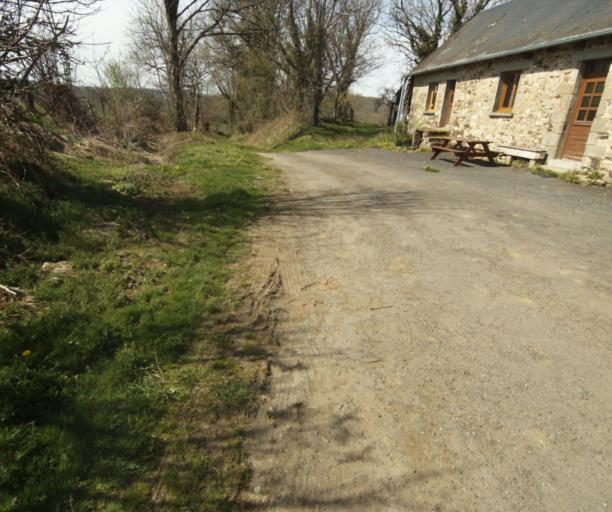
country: FR
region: Limousin
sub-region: Departement de la Correze
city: Naves
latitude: 45.3701
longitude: 1.7740
